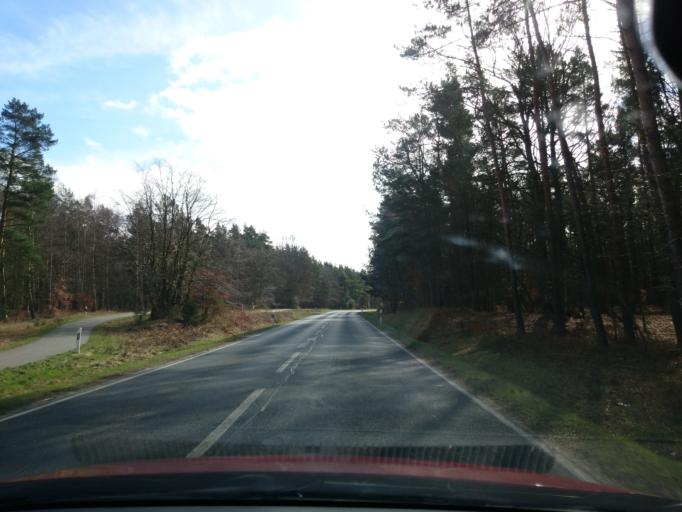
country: DE
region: Mecklenburg-Vorpommern
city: Ostseebad Prerow
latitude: 54.4213
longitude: 12.5744
